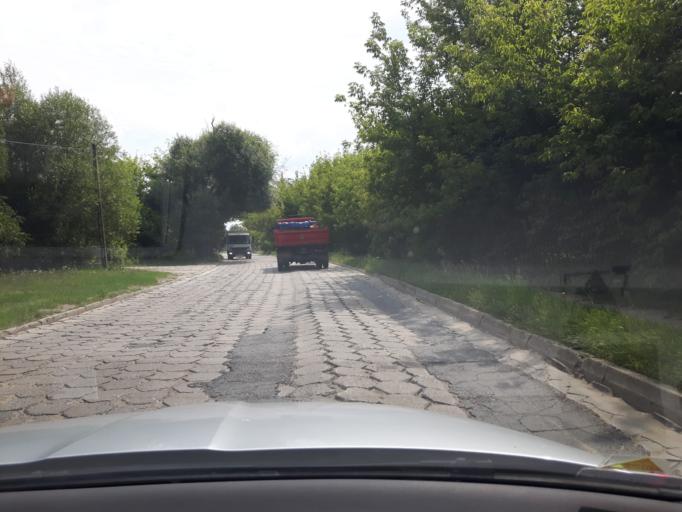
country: PL
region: Masovian Voivodeship
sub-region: Warszawa
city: Wilanow
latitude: 52.1995
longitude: 21.0794
